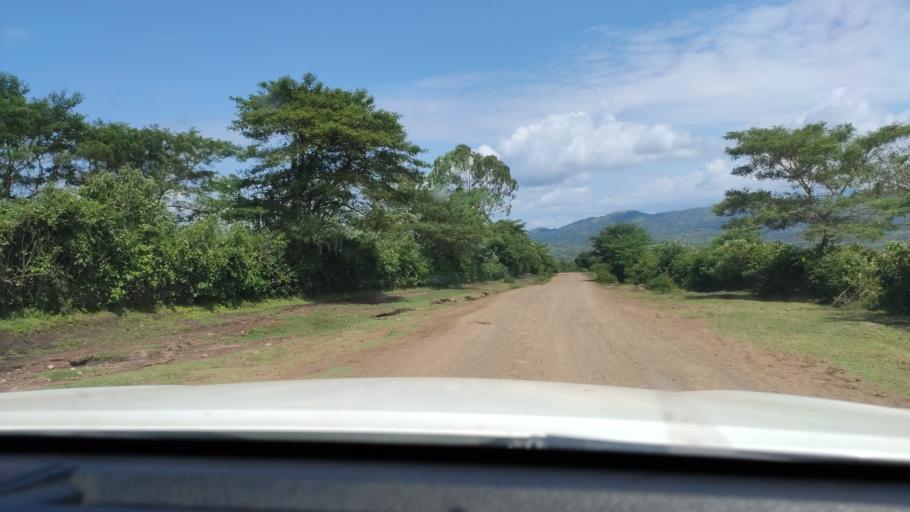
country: ET
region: Southern Nations, Nationalities, and People's Region
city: Felege Neway
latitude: 6.3653
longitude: 36.9850
